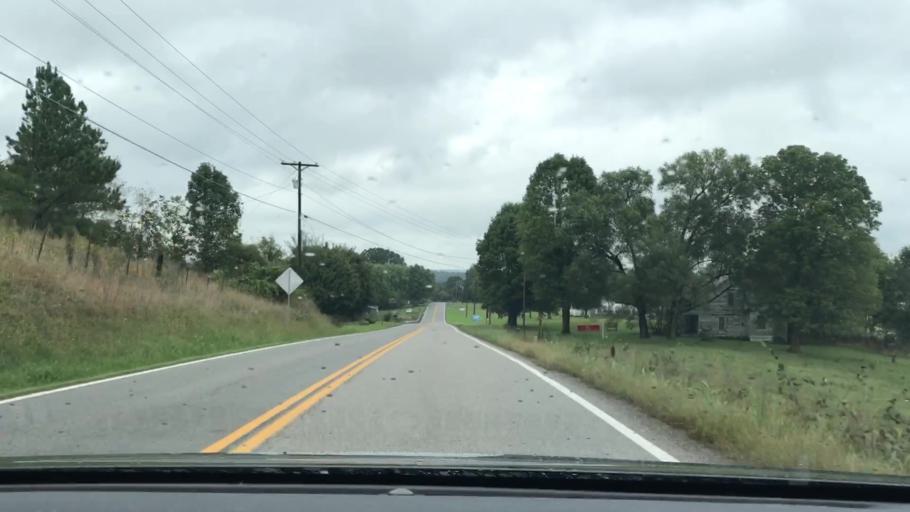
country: US
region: Kentucky
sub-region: Monroe County
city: Tompkinsville
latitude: 36.6568
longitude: -85.7426
